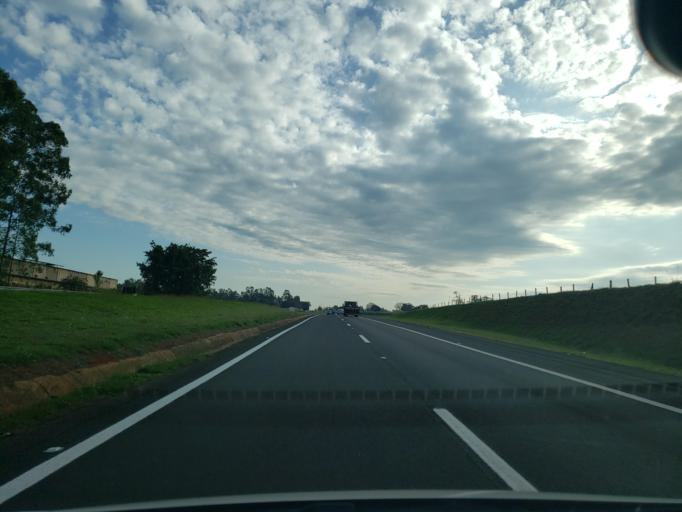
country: BR
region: Sao Paulo
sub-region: Guararapes
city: Guararapes
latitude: -21.2080
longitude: -50.6551
